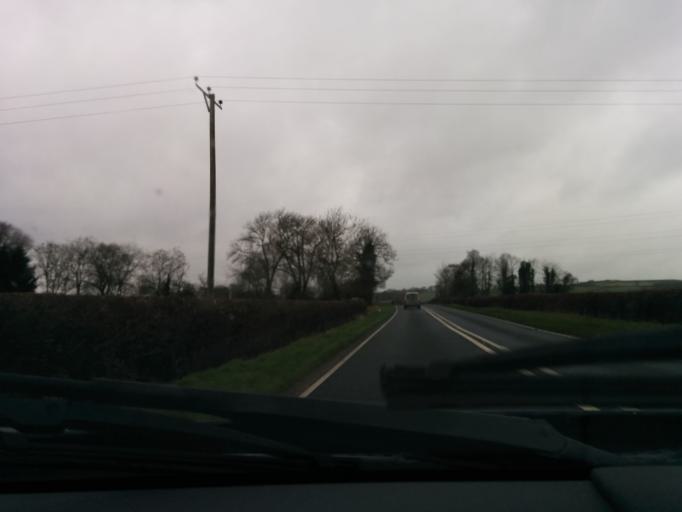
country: GB
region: England
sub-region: Oxfordshire
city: Eynsham
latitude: 51.7578
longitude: -1.3395
